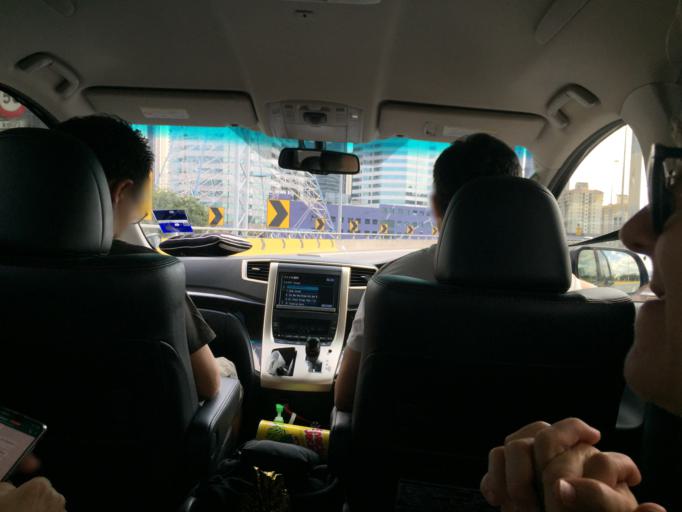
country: MY
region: Kuala Lumpur
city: Kuala Lumpur
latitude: 3.1162
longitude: 101.6647
